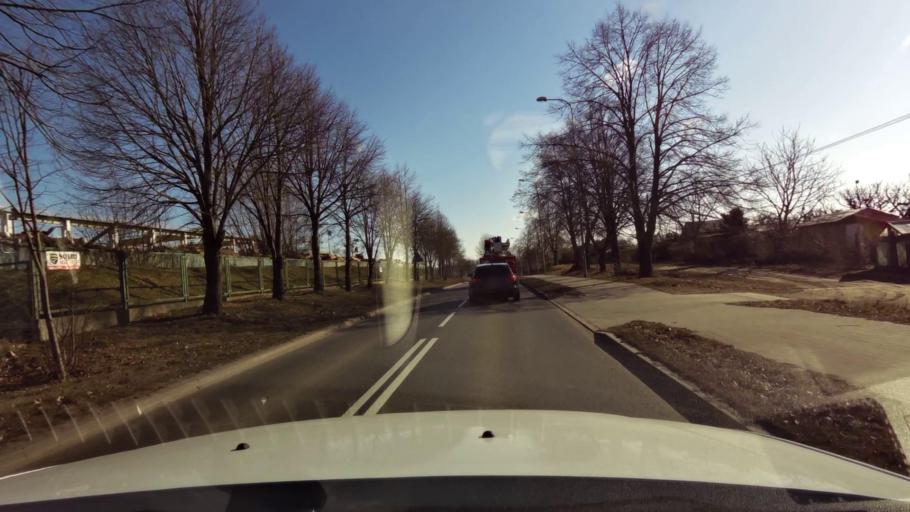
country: PL
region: West Pomeranian Voivodeship
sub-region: Powiat mysliborski
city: Barlinek
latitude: 52.9915
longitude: 15.1988
